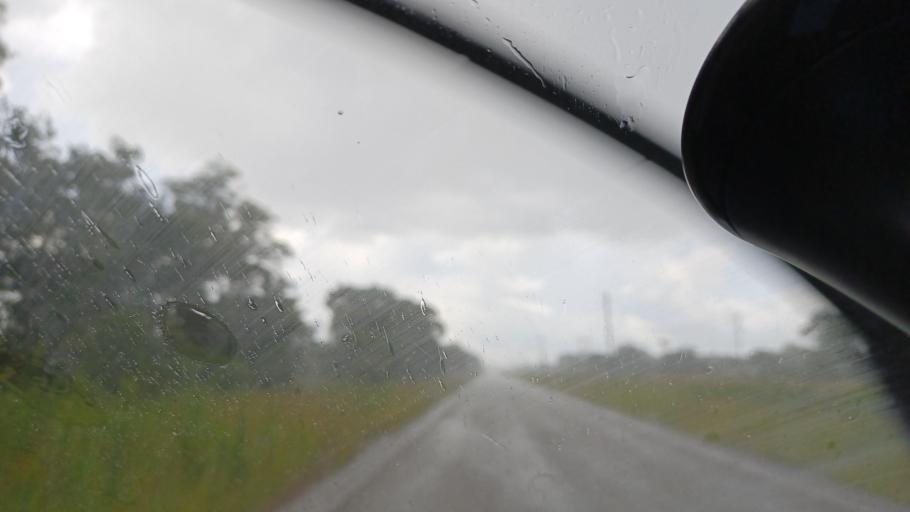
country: ZM
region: North-Western
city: Kasempa
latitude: -13.0955
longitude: 25.9132
